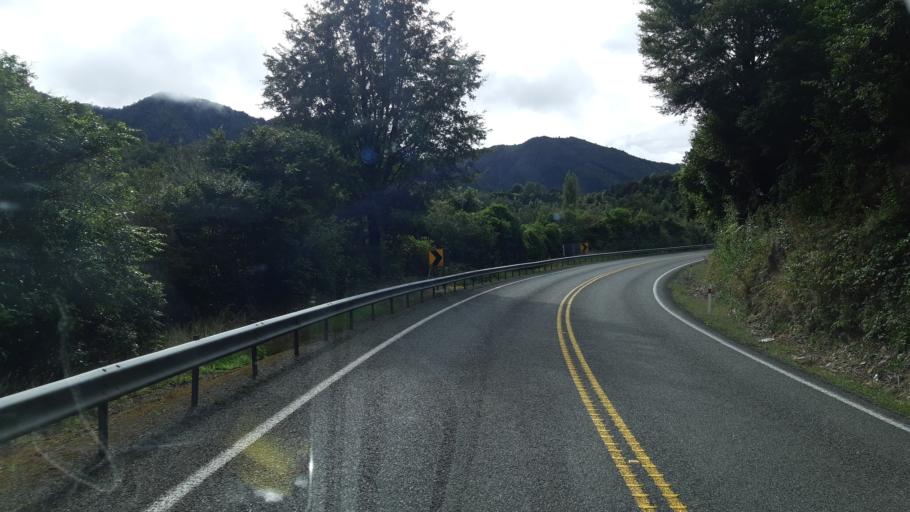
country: NZ
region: West Coast
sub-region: Buller District
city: Westport
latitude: -41.7690
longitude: 172.2309
